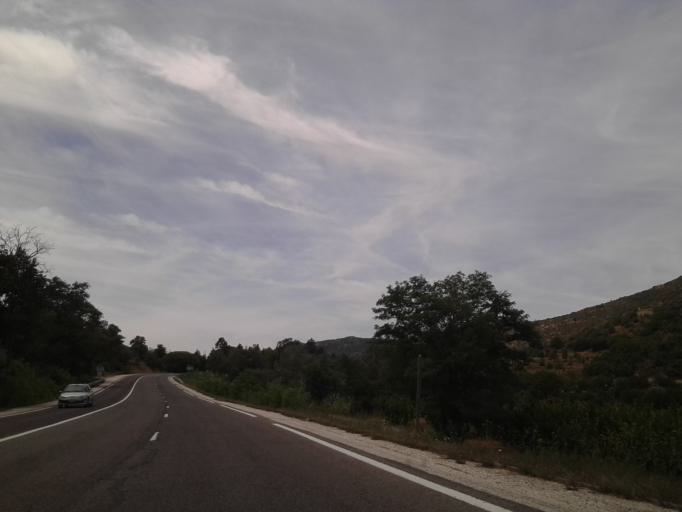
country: FR
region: Languedoc-Roussillon
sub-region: Departement des Pyrenees-Orientales
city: Vinca
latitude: 42.6524
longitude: 2.5518
